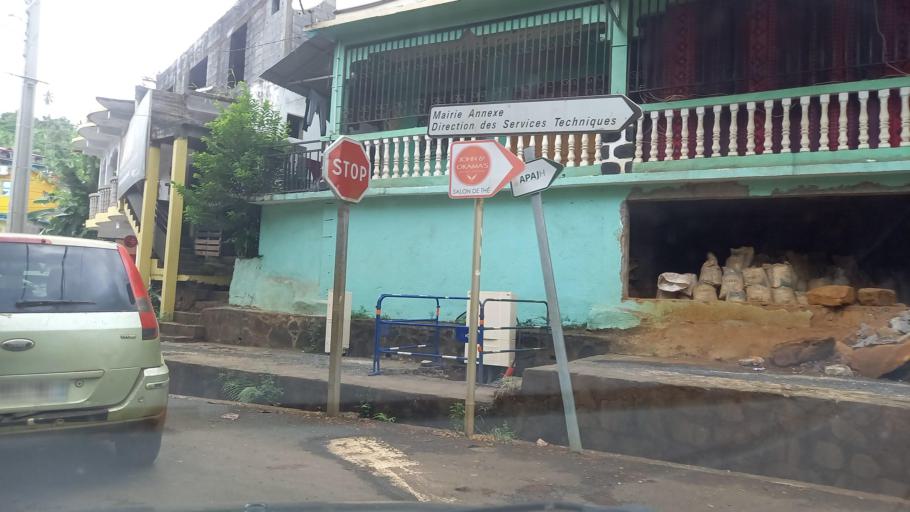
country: YT
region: Chiconi
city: Chiconi
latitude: -12.8448
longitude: 45.1159
